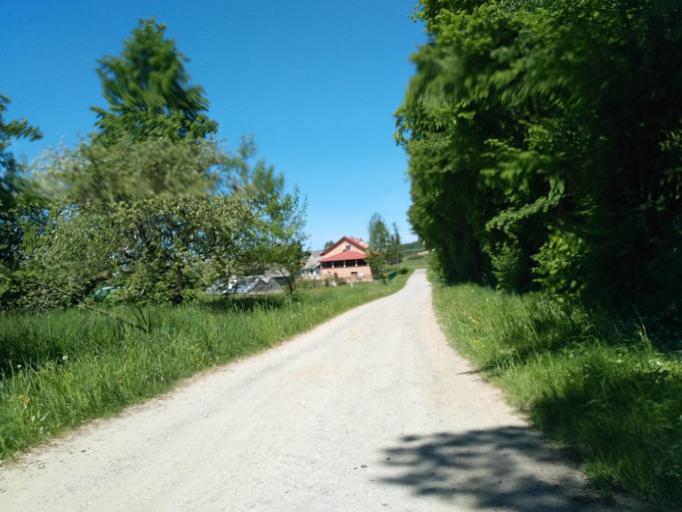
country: PL
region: Subcarpathian Voivodeship
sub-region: Powiat sanocki
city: Dlugie
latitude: 49.6068
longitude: 22.0353
